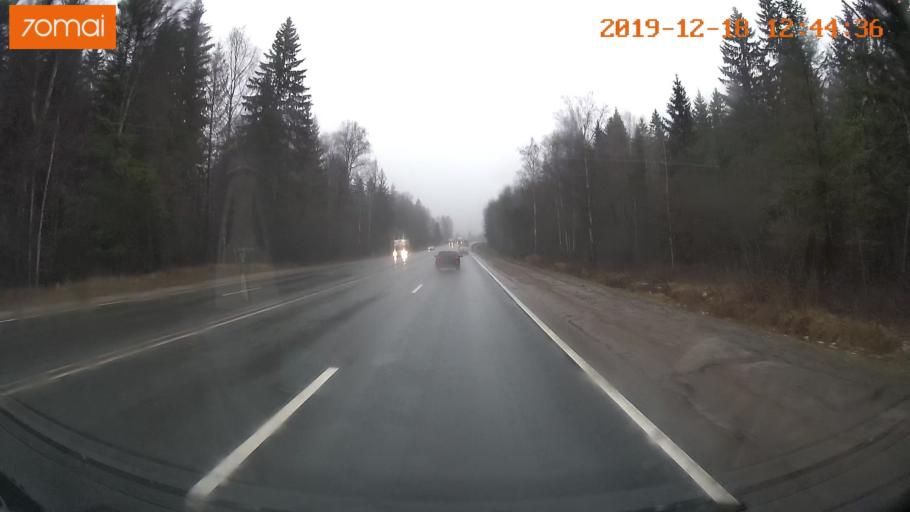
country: RU
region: Moskovskaya
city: Vysokovsk
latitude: 56.2216
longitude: 36.6498
